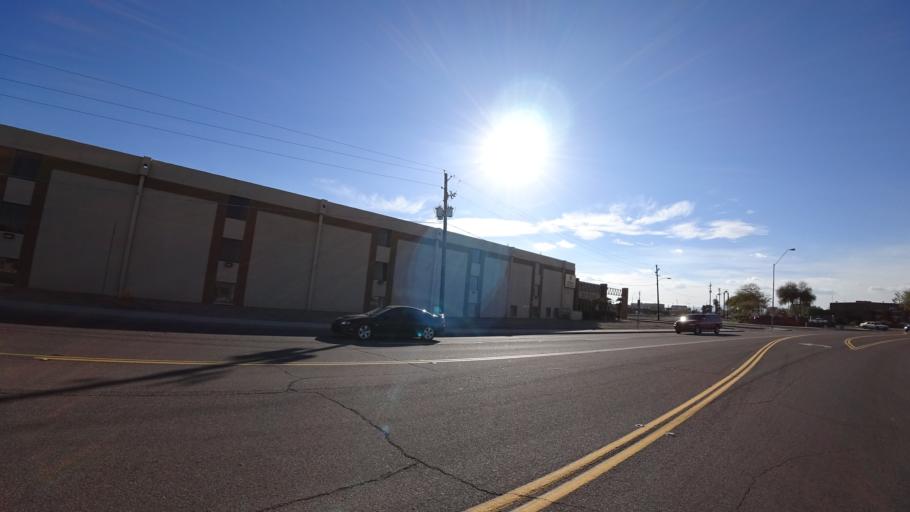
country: US
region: Arizona
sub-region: Maricopa County
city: Peoria
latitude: 33.5811
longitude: -112.2343
